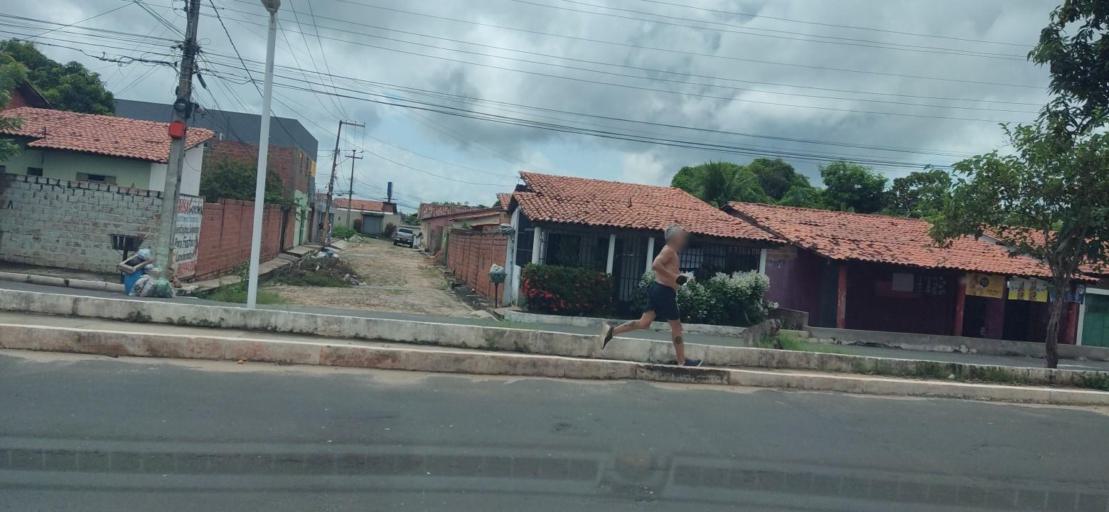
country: BR
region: Piaui
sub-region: Teresina
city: Teresina
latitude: -5.0660
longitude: -42.7516
